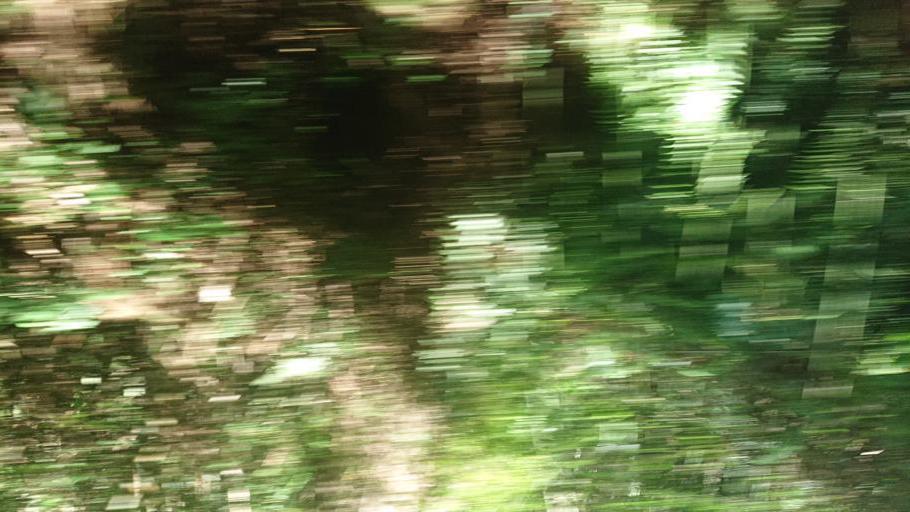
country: TW
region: Taiwan
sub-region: Yunlin
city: Douliu
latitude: 23.5304
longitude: 120.6588
